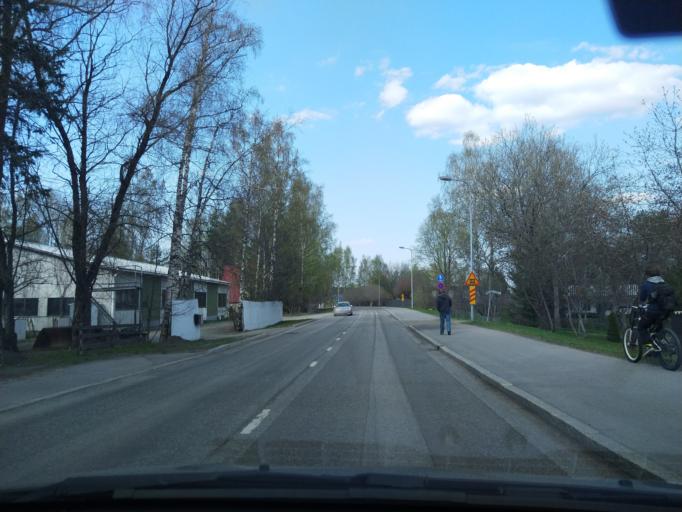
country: FI
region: Uusimaa
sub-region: Helsinki
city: Lohja
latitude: 60.1934
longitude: 24.0016
